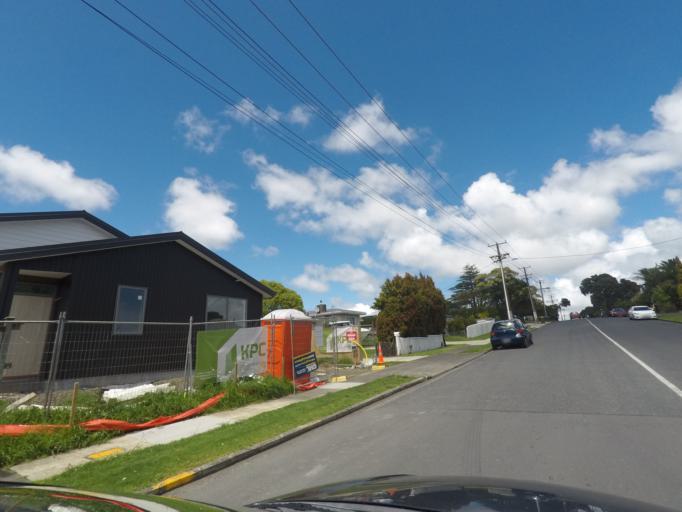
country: NZ
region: Auckland
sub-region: Auckland
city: Rosebank
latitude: -36.8776
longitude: 174.6427
